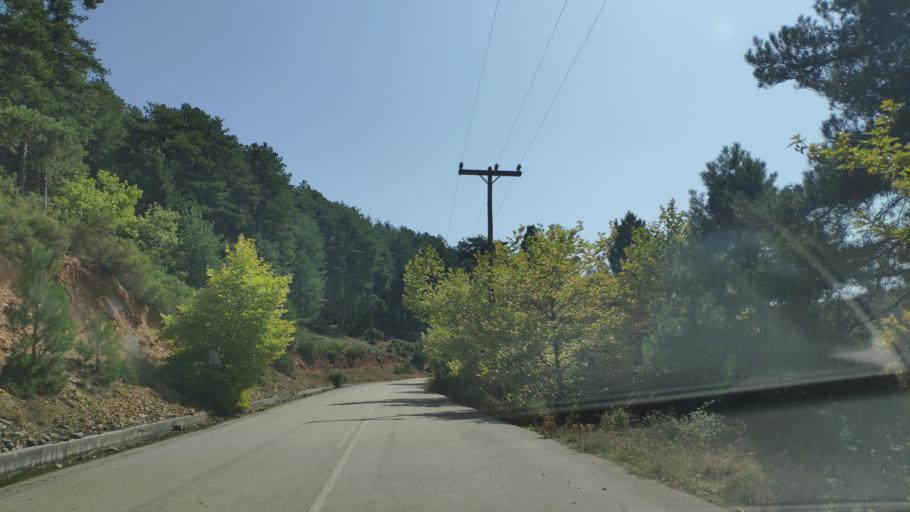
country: GR
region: West Greece
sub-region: Nomos Achaias
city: Kalavryta
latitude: 37.9290
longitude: 22.2907
